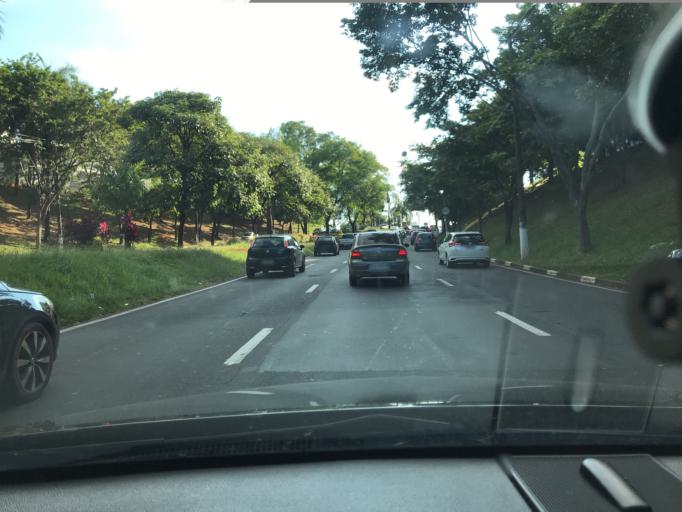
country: BR
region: Sao Paulo
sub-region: Campinas
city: Campinas
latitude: -22.9165
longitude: -47.0605
